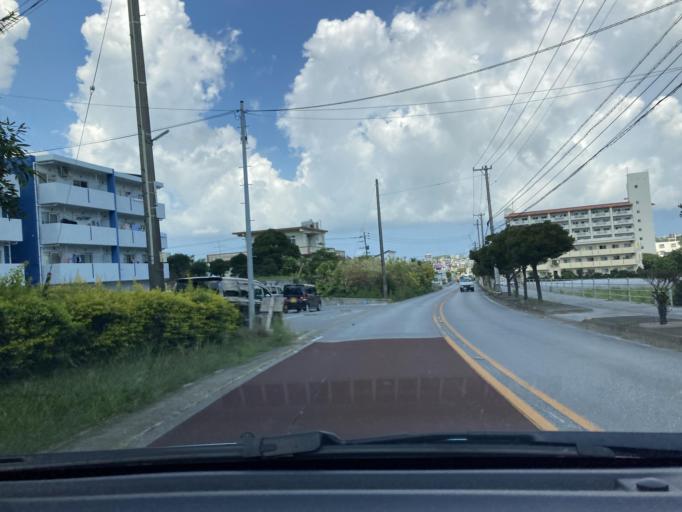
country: JP
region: Okinawa
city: Tomigusuku
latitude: 26.1500
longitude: 127.7532
